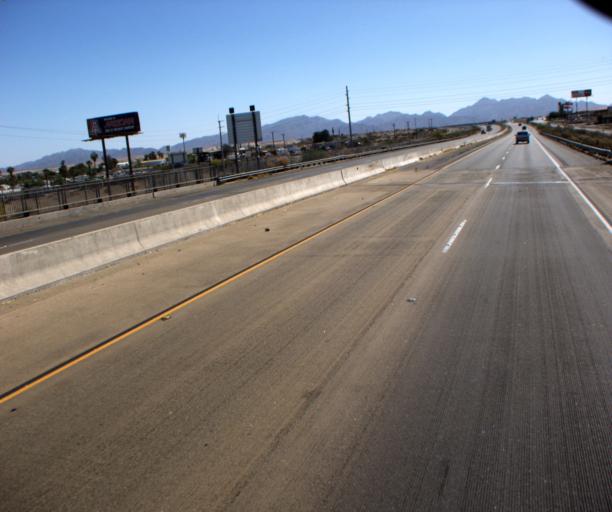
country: US
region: Arizona
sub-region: La Paz County
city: Ehrenberg
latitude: 33.6043
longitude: -114.5297
